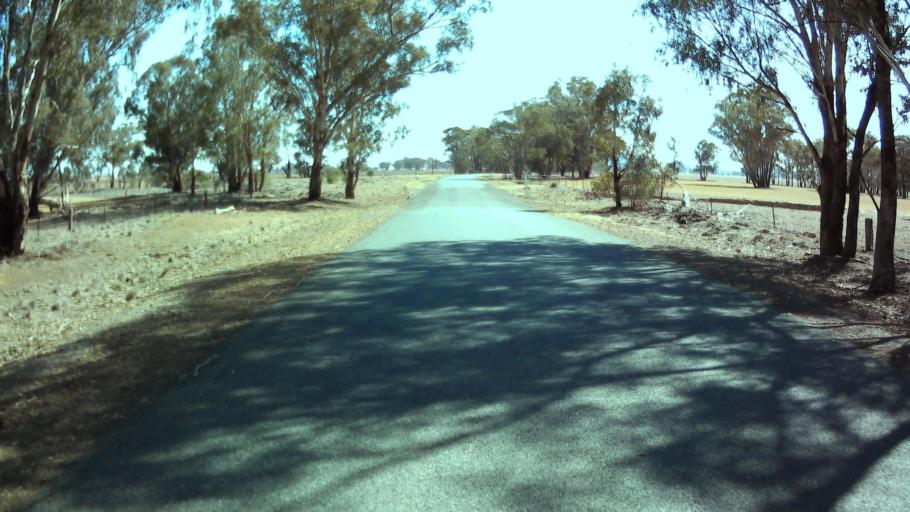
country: AU
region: New South Wales
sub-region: Weddin
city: Grenfell
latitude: -33.7301
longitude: 147.8894
